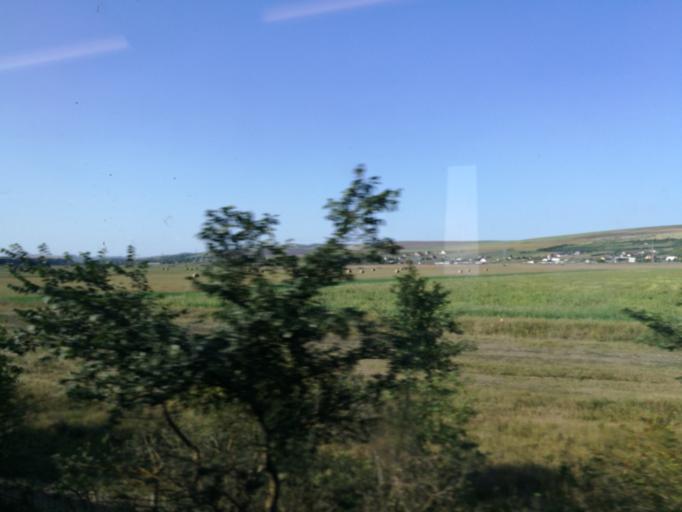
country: RO
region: Vaslui
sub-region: Municipiul Vaslui
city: Brodoc
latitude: 46.6654
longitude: 27.6769
